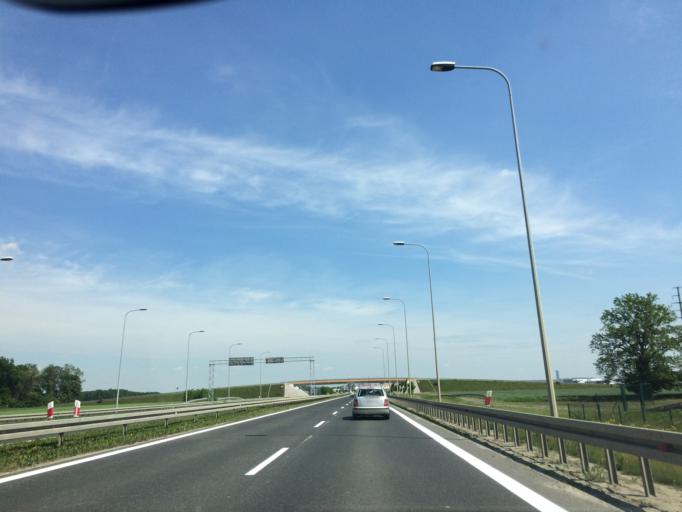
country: PL
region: Lower Silesian Voivodeship
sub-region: Powiat wroclawski
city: Tyniec Maly
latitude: 51.0254
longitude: 16.9081
